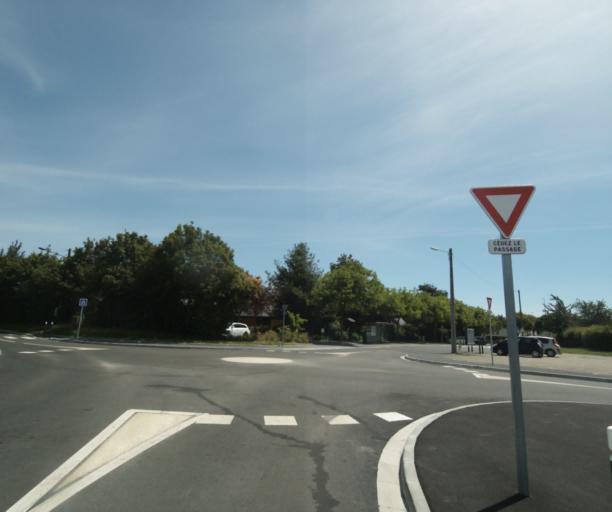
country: FR
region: Pays de la Loire
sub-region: Departement de la Mayenne
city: Change
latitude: 48.0815
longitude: -0.8038
